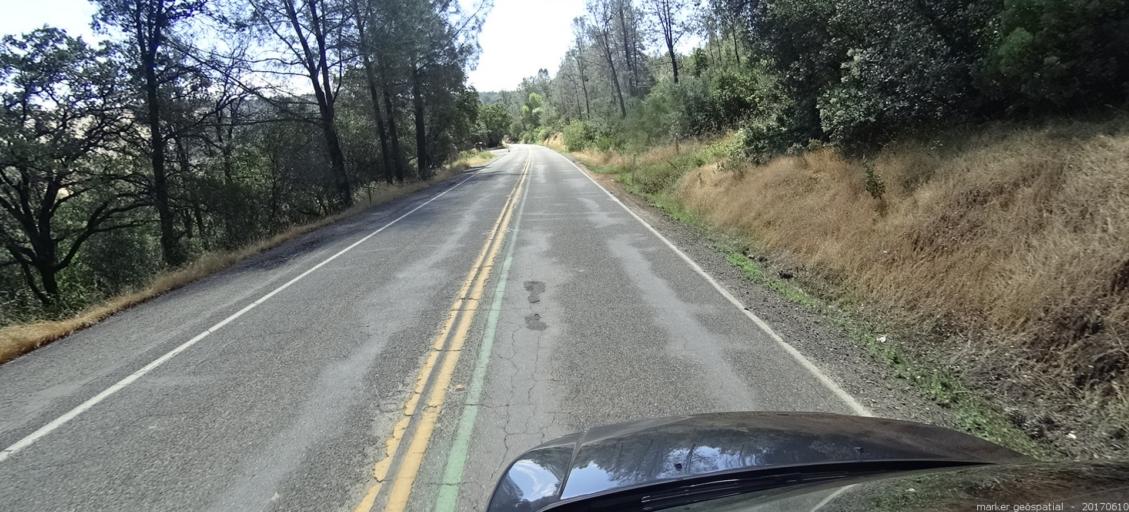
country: US
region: California
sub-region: Butte County
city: Oroville East
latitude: 39.5334
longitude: -121.5030
